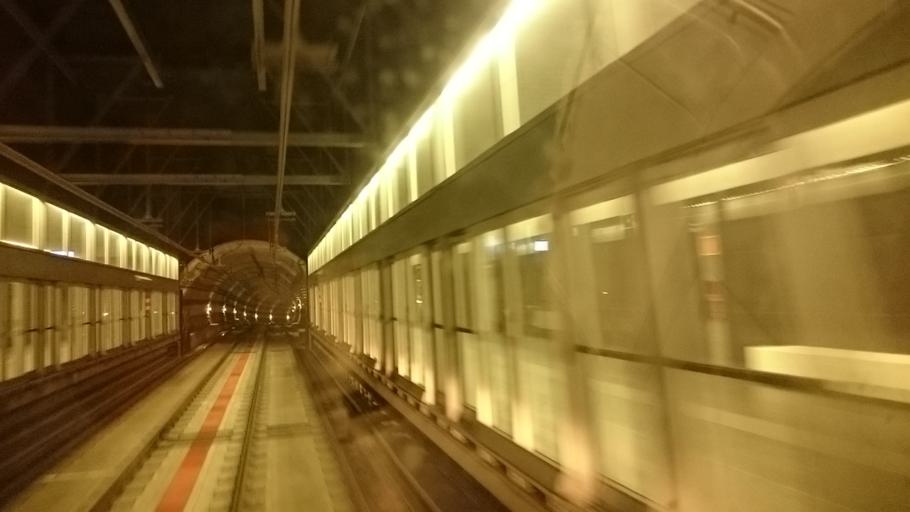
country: ES
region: Catalonia
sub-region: Provincia de Barcelona
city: El Prat de Llobregat
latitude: 41.3301
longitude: 2.1024
